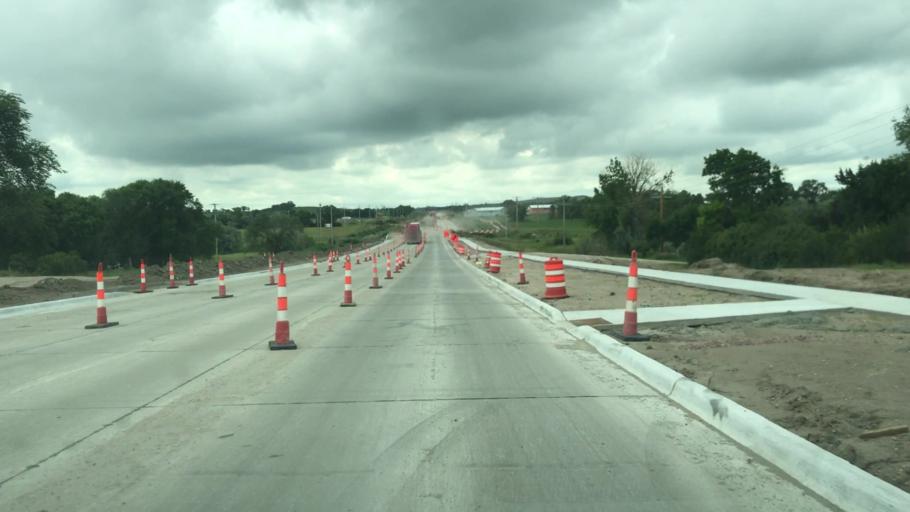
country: US
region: South Dakota
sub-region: Todd County
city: Mission
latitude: 43.3045
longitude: -100.6527
